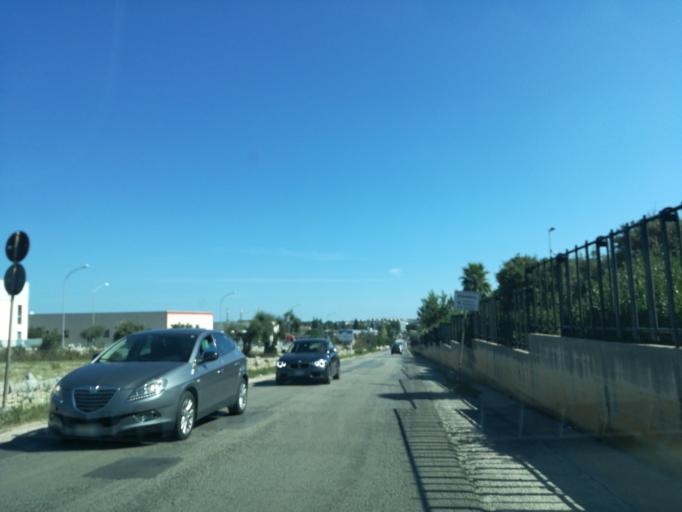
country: IT
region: Apulia
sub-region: Provincia di Bari
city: Castellana
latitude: 40.8843
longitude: 17.1551
